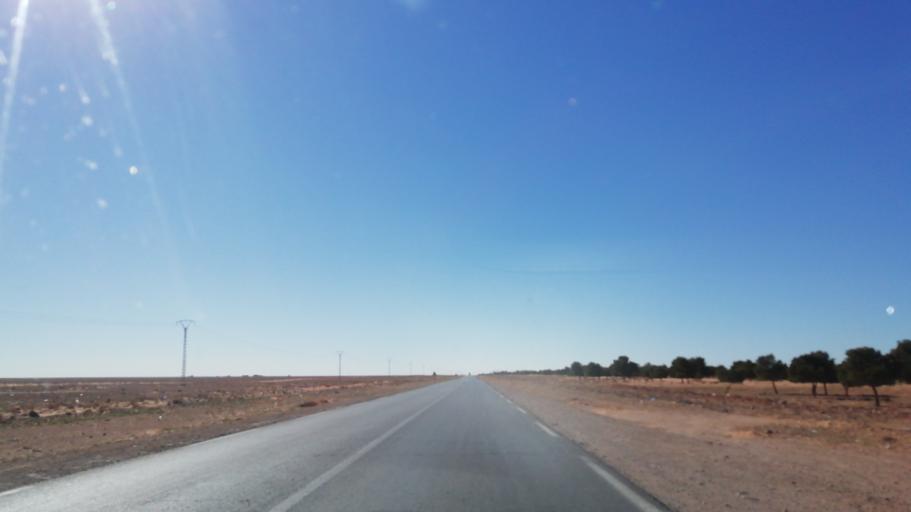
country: DZ
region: Saida
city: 'Ain el Hadjar
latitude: 34.0002
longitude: 0.0429
